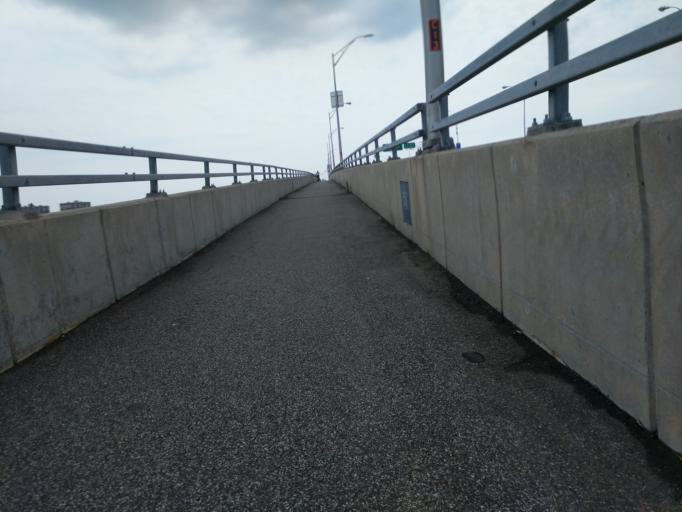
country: US
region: New York
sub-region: Nassau County
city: Inwood
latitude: 40.5936
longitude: -73.8202
